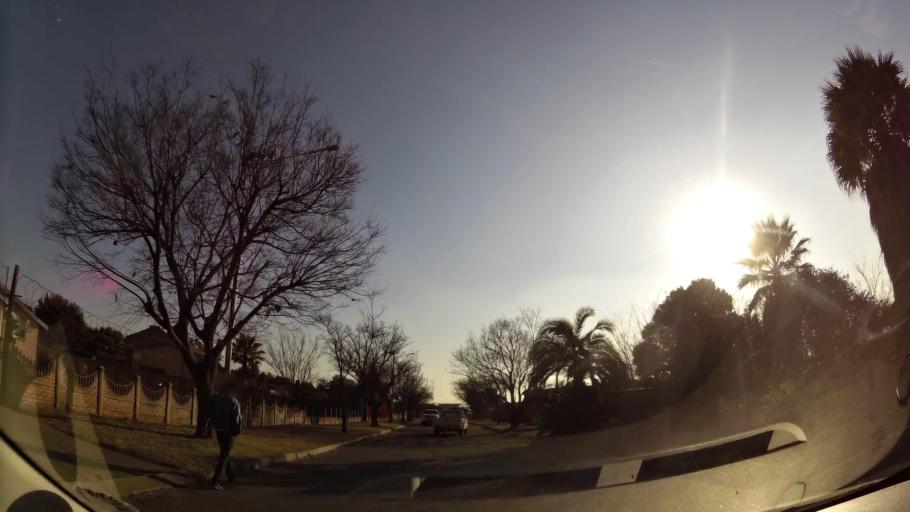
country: ZA
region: Gauteng
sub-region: West Rand District Municipality
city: Randfontein
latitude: -26.2002
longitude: 27.6997
